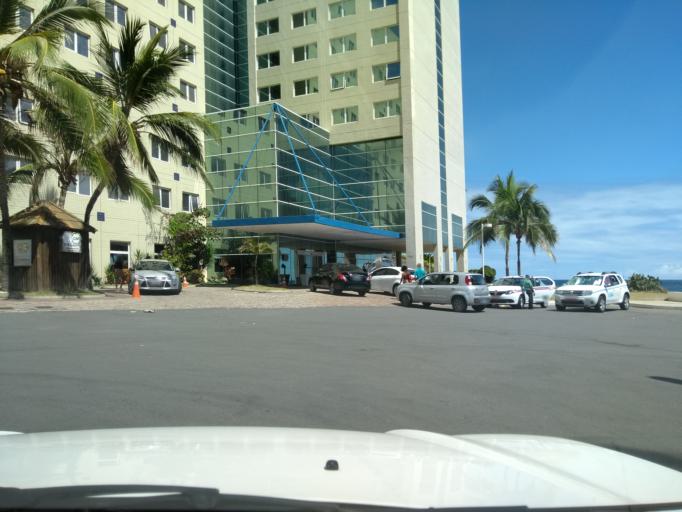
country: BR
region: Bahia
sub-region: Salvador
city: Salvador
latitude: -13.0150
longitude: -38.4854
